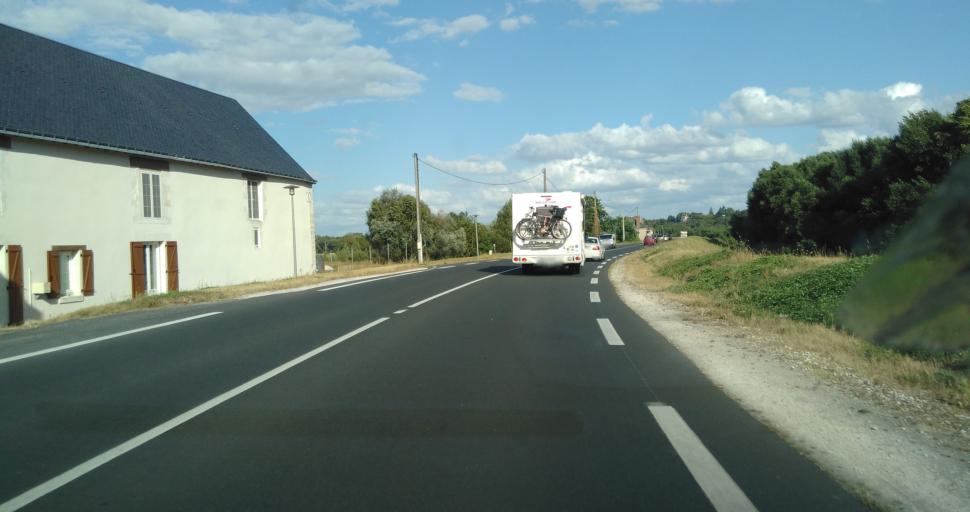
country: FR
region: Centre
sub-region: Departement d'Indre-et-Loire
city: Montlouis-sur-Loire
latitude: 47.3957
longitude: 0.8292
